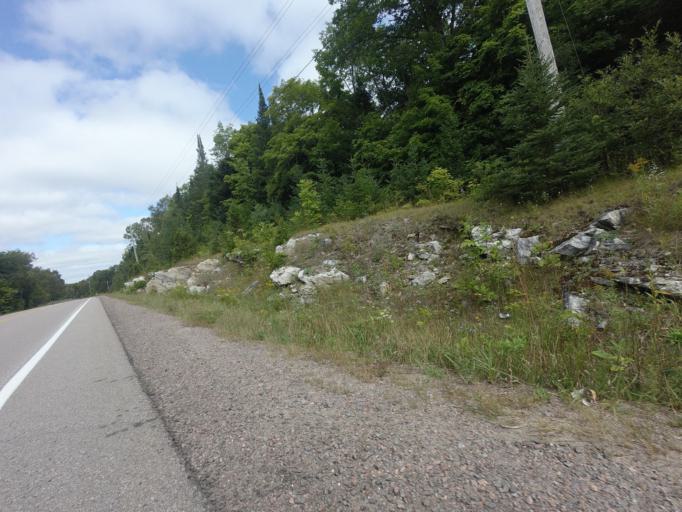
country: CA
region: Ontario
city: Bancroft
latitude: 44.9433
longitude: -78.2984
